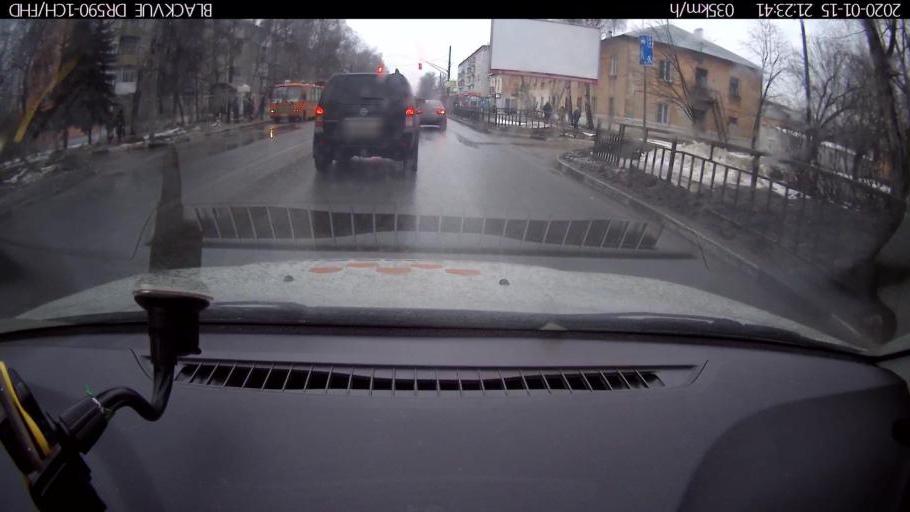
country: RU
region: Nizjnij Novgorod
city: Nizhniy Novgorod
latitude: 56.3176
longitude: 43.8687
